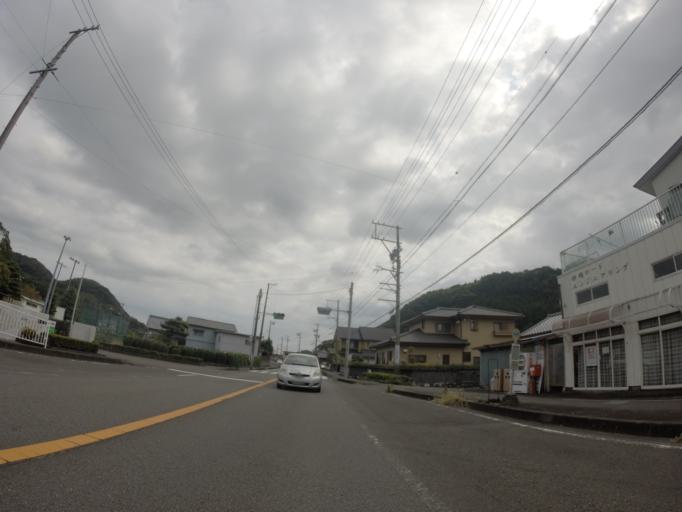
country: JP
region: Shizuoka
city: Fujieda
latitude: 34.8814
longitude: 138.2175
